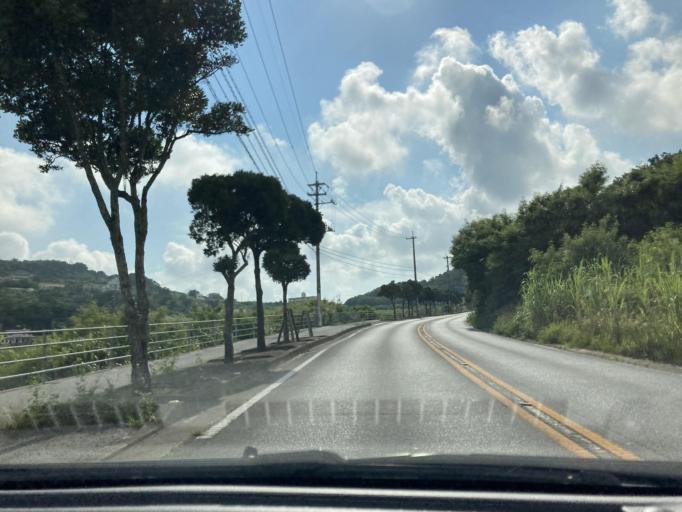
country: JP
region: Okinawa
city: Tomigusuku
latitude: 26.1495
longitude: 127.7544
